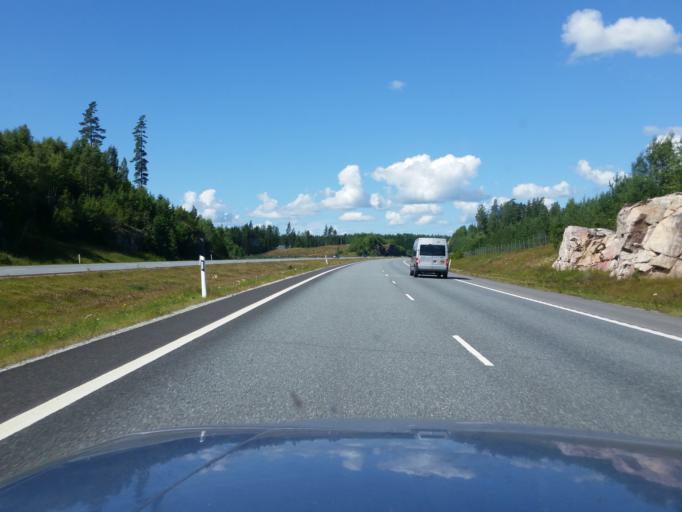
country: FI
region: Varsinais-Suomi
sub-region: Salo
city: Pertteli
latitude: 60.3994
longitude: 23.2415
